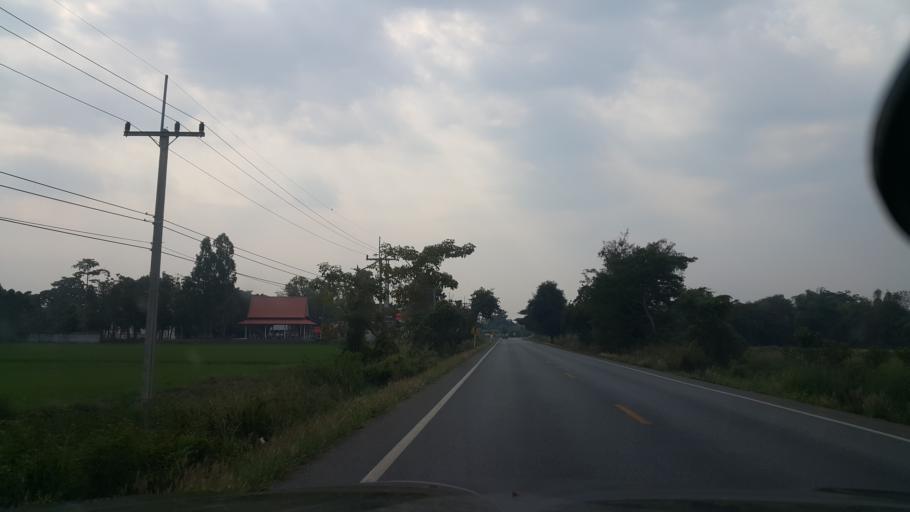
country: TH
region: Sukhothai
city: Si Samrong
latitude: 17.1187
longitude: 99.8900
